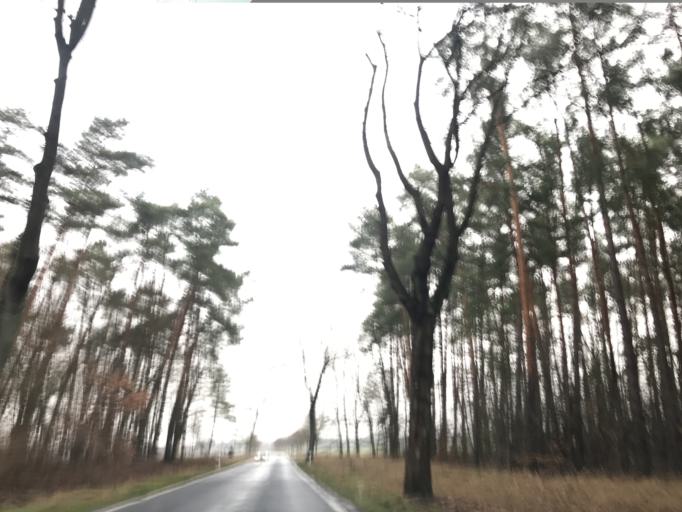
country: DE
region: Brandenburg
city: Brieselang
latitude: 52.6651
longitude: 12.9793
